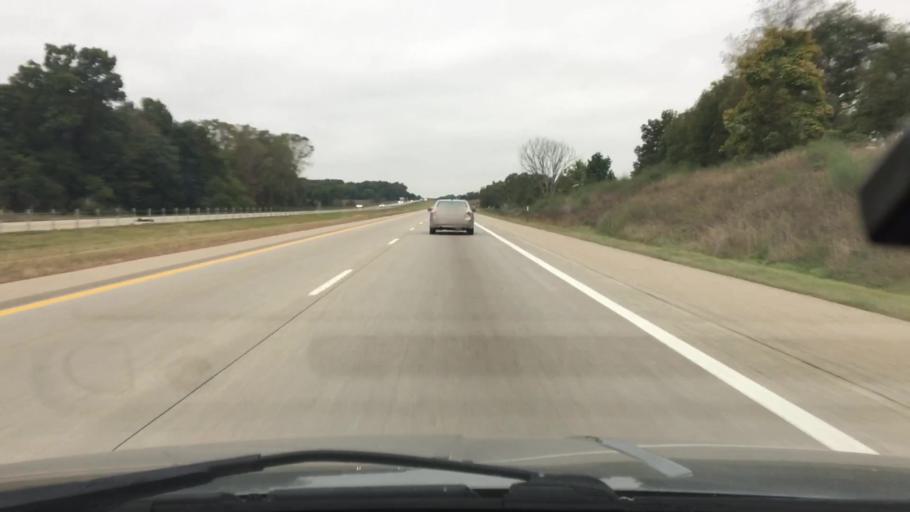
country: US
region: Michigan
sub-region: Van Buren County
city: Mattawan
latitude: 42.2197
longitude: -85.8294
